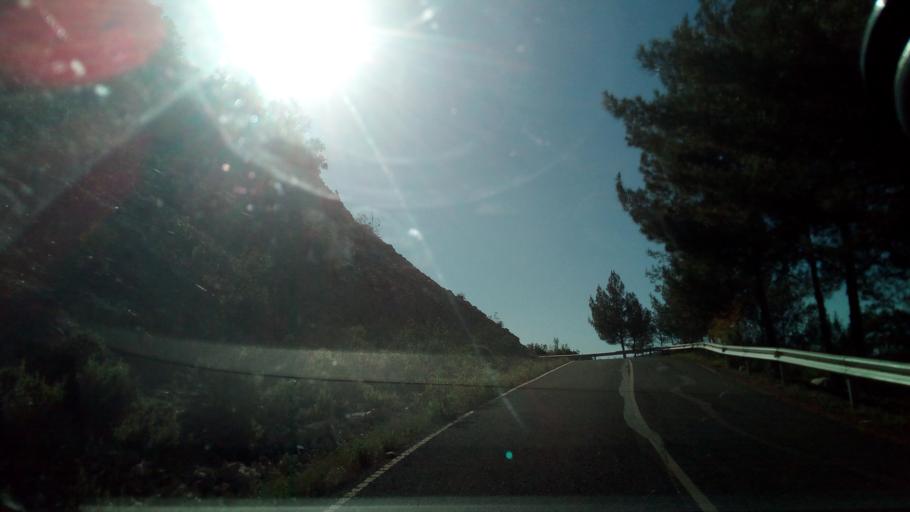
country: CY
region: Limassol
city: Pachna
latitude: 34.8731
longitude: 32.7510
